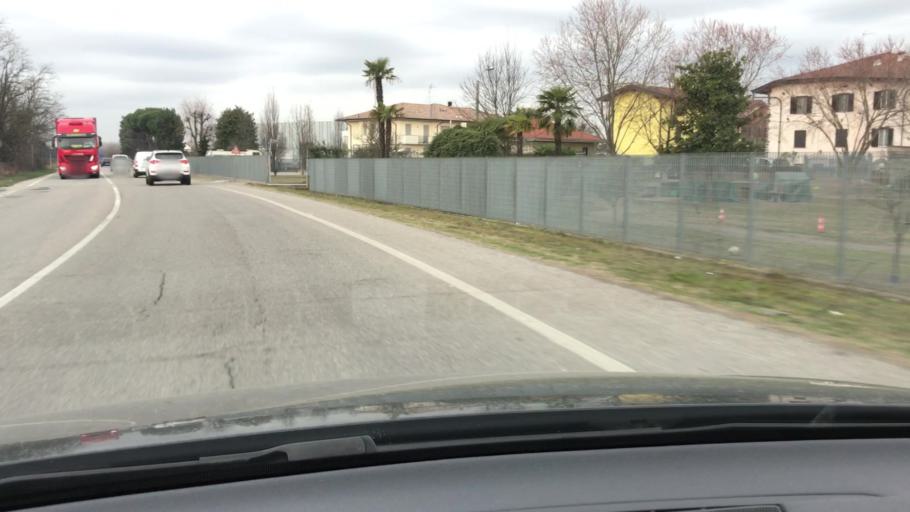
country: IT
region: Lombardy
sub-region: Provincia di Pavia
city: Cassolnovo
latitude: 45.3567
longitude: 8.8130
